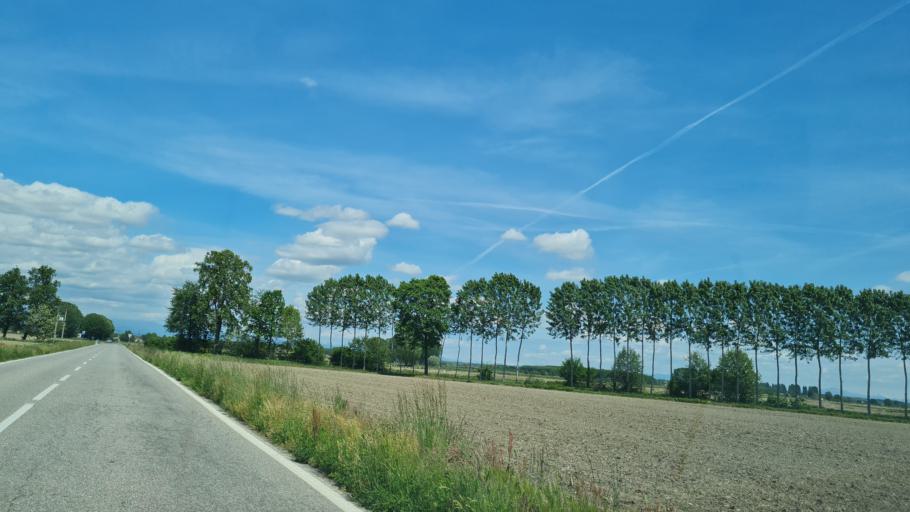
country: IT
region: Piedmont
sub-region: Provincia di Novara
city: Sillavengo
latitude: 45.5052
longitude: 8.4433
